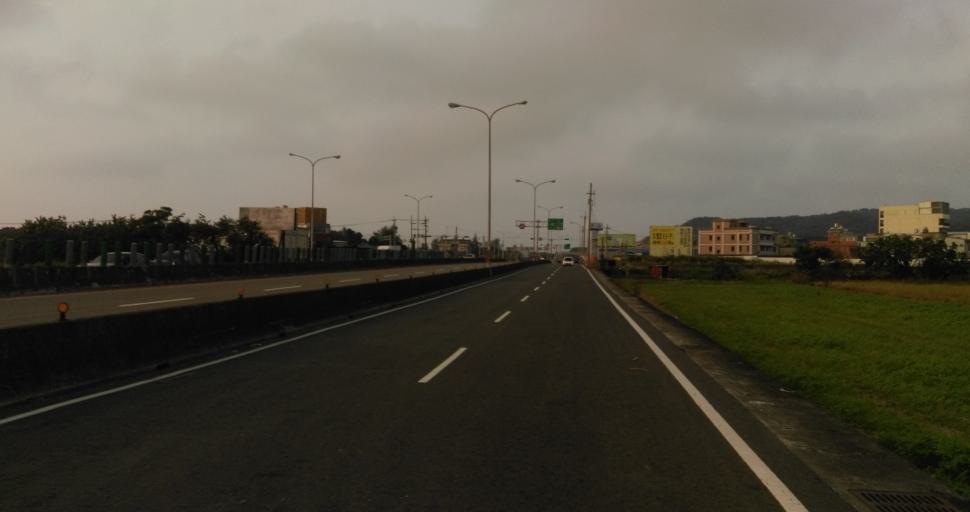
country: TW
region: Taiwan
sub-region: Hsinchu
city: Zhubei
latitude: 24.8711
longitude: 120.9534
